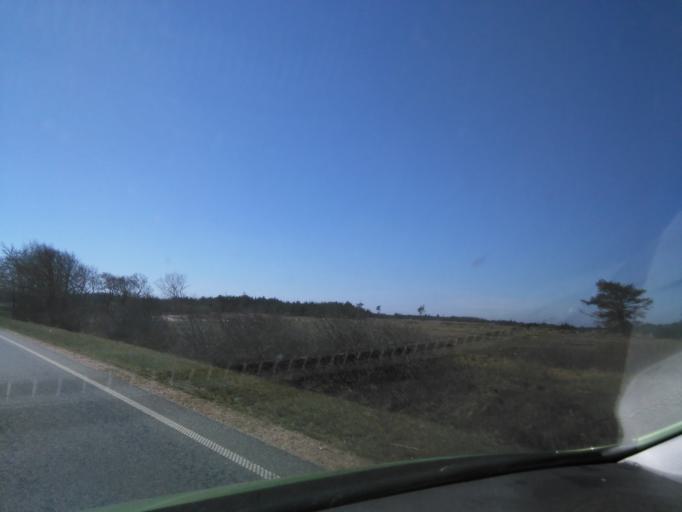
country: DK
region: South Denmark
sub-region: Varde Kommune
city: Oksbol
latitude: 55.6116
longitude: 8.2294
